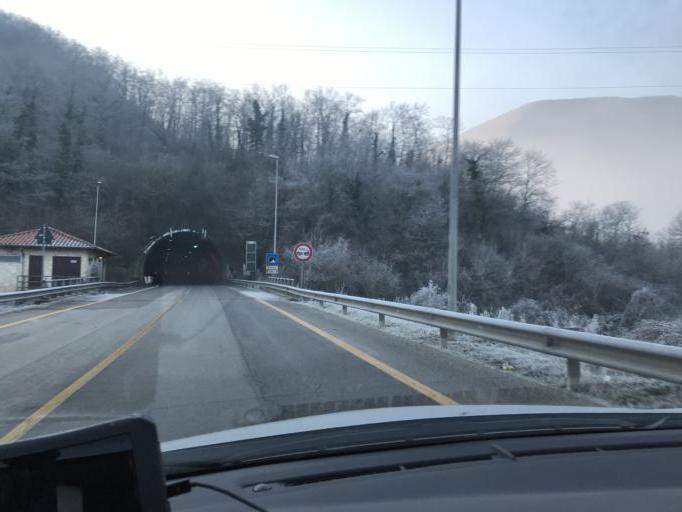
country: IT
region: Latium
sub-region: Provincia di Rieti
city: Colli sul Velino
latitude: 42.5036
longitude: 12.7468
